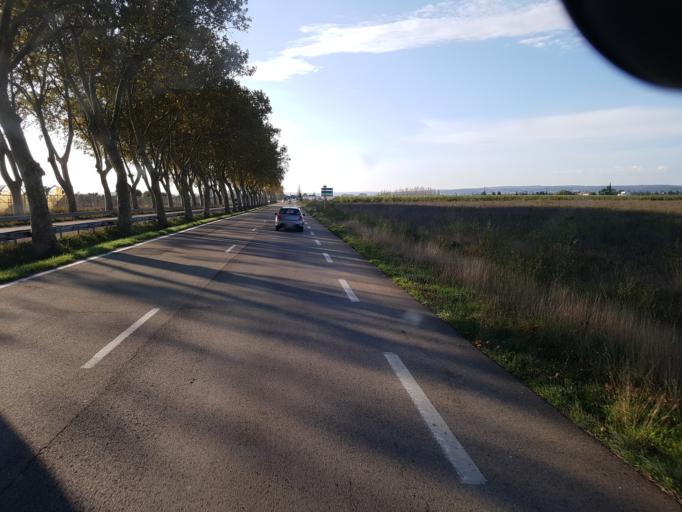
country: FR
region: Languedoc-Roussillon
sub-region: Departement du Gard
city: Manduel
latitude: 43.8299
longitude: 4.4602
